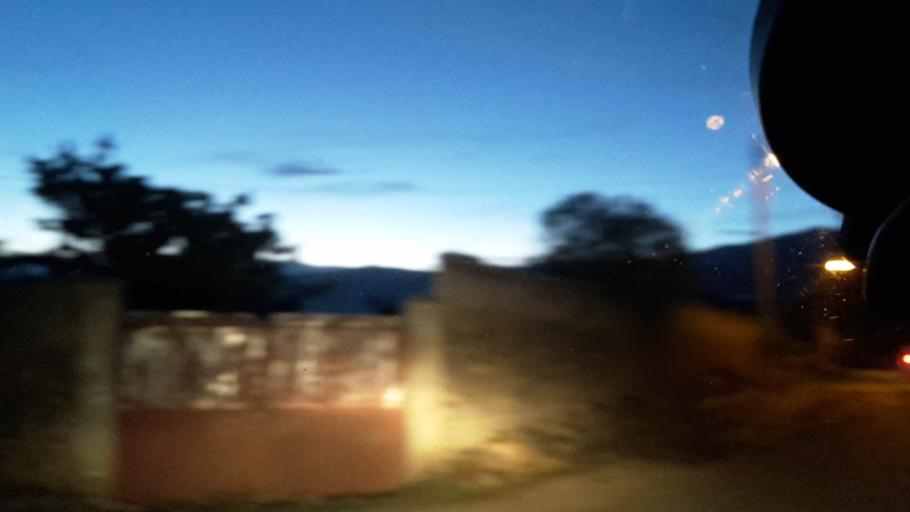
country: BO
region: Cochabamba
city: Cochabamba
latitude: -17.3282
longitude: -66.2166
